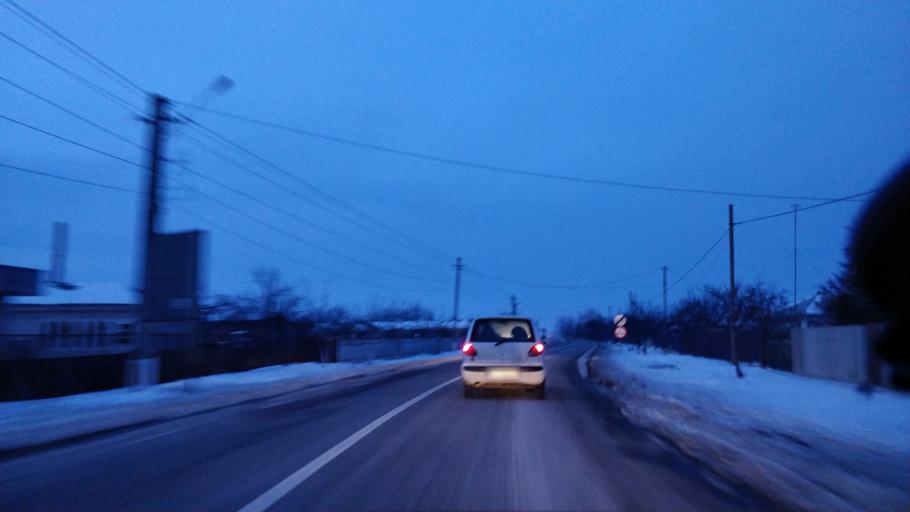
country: RO
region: Vrancea
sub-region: Comuna Nanesti
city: Nanesti
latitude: 45.5526
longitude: 27.5001
